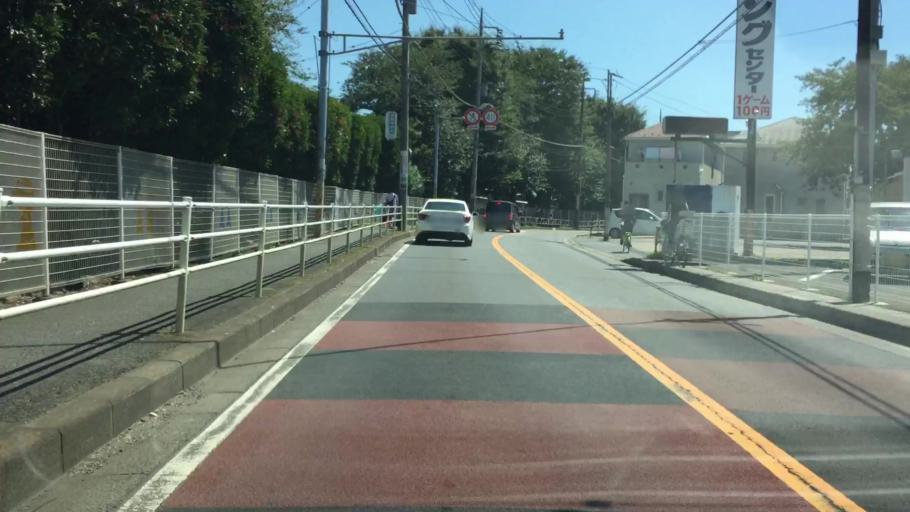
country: JP
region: Chiba
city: Funabashi
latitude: 35.7298
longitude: 139.9942
